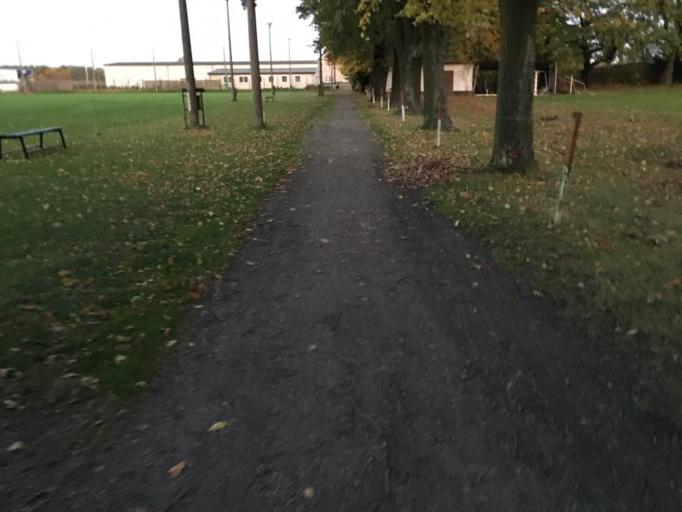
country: DE
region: Brandenburg
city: Tschernitz
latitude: 51.5749
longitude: 14.6173
